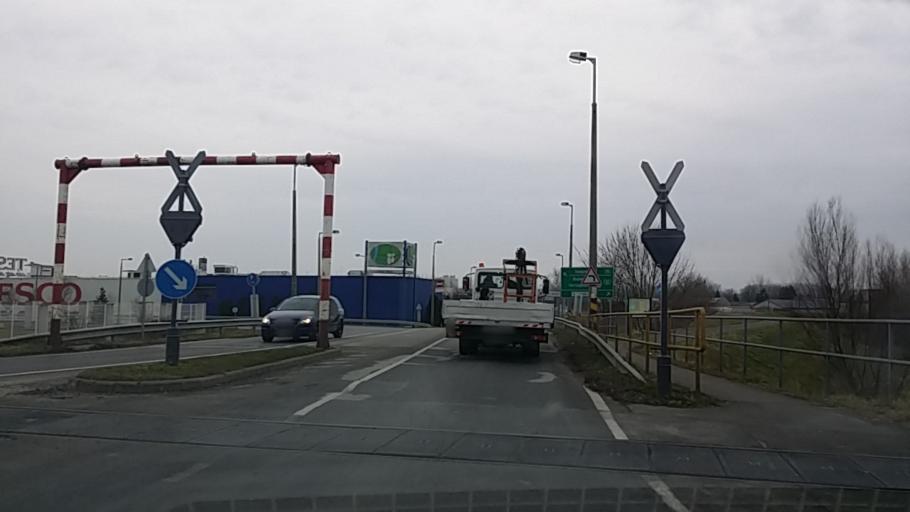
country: HU
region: Bacs-Kiskun
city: Baja
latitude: 46.1924
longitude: 18.9336
